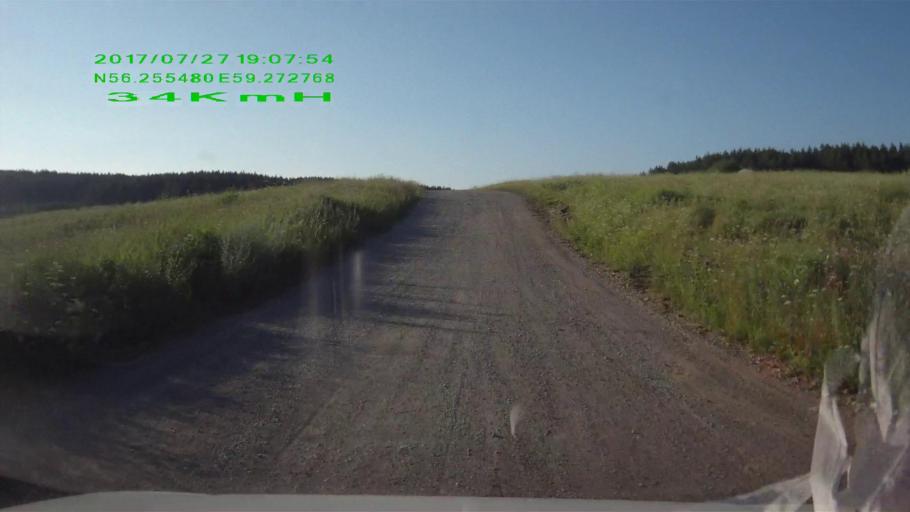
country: RU
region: Sverdlovsk
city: Mikhaylovsk
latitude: 56.2559
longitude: 59.2724
